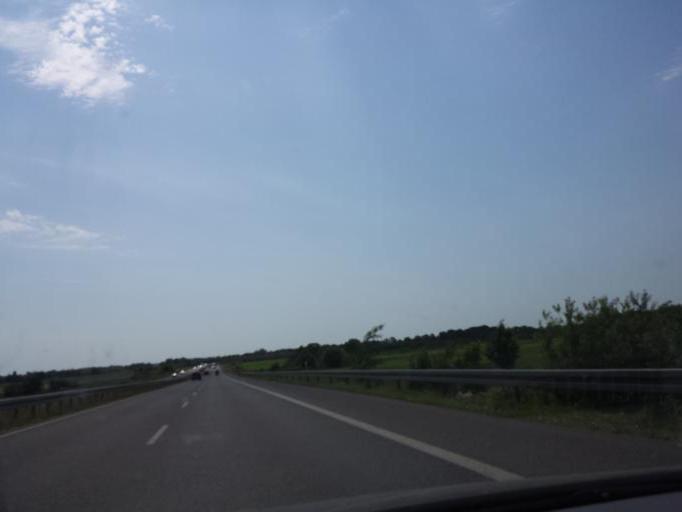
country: DE
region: Brandenburg
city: Oranienburg
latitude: 52.7744
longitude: 13.2180
